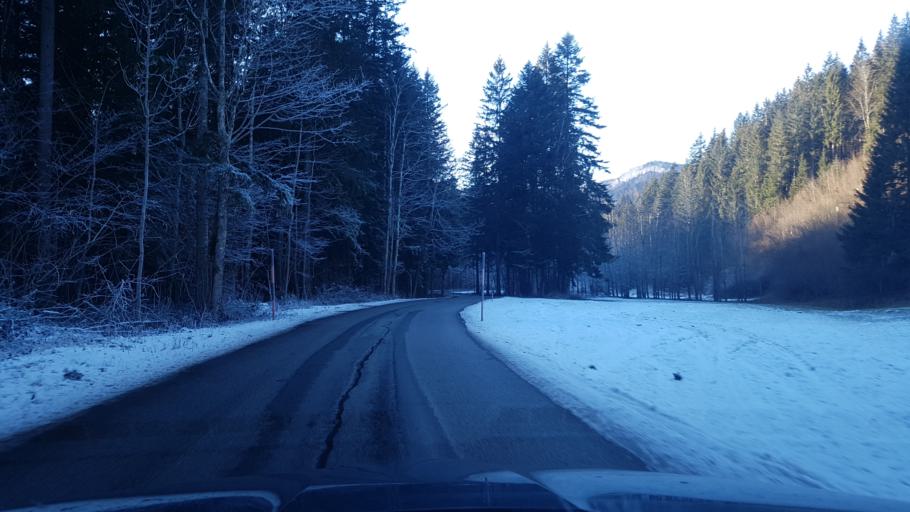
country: AT
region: Salzburg
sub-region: Politischer Bezirk Hallein
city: Abtenau
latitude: 47.5835
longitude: 13.3530
